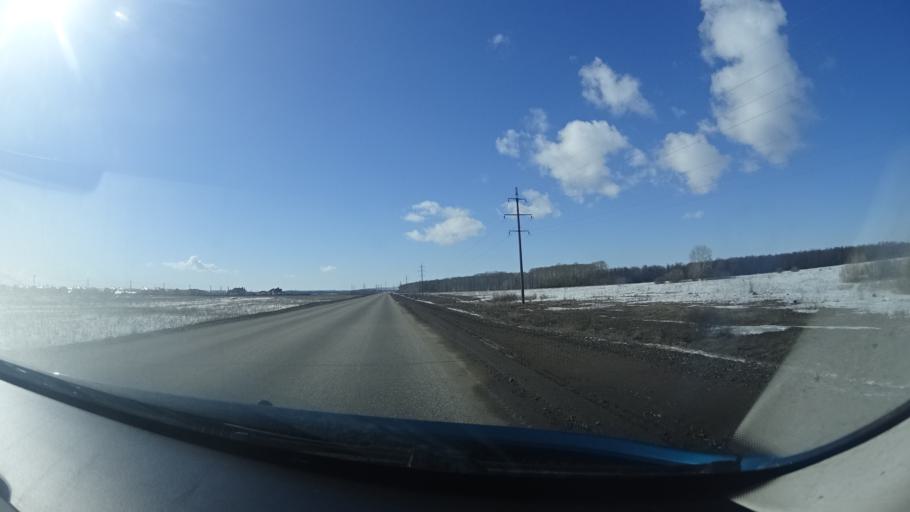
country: RU
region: Bashkortostan
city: Ufa
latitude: 54.6318
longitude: 55.9042
